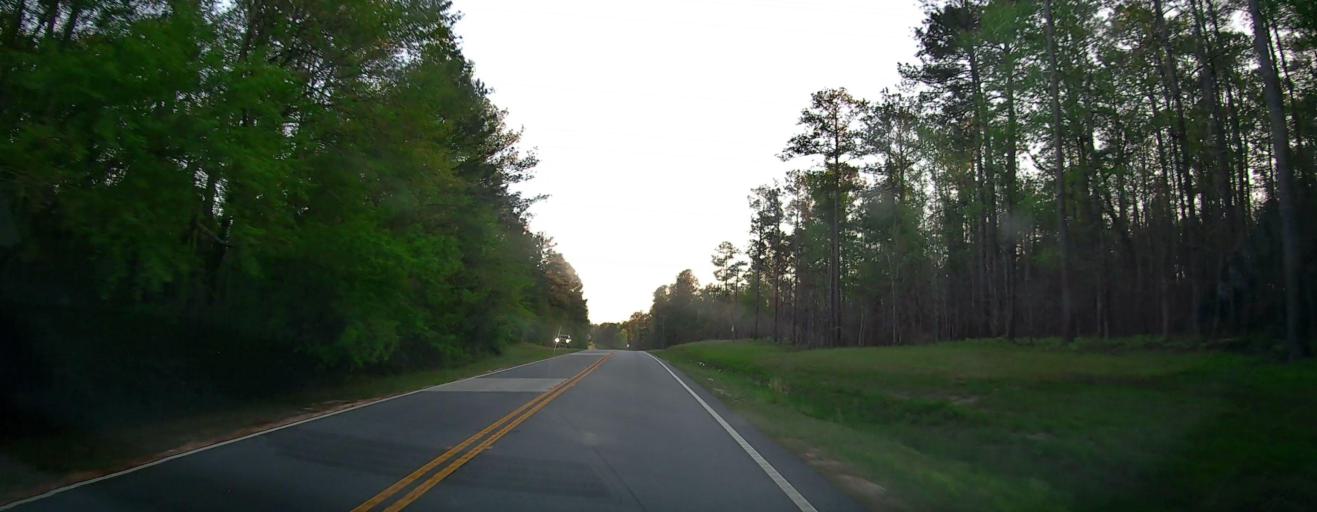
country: US
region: Georgia
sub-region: Talbot County
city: Talbotton
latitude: 32.5193
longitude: -84.6044
